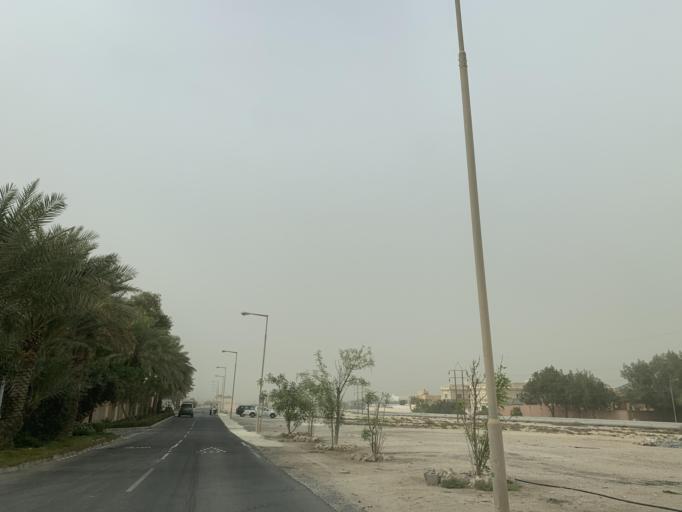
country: BH
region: Northern
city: Ar Rifa'
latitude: 26.1413
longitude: 50.5351
